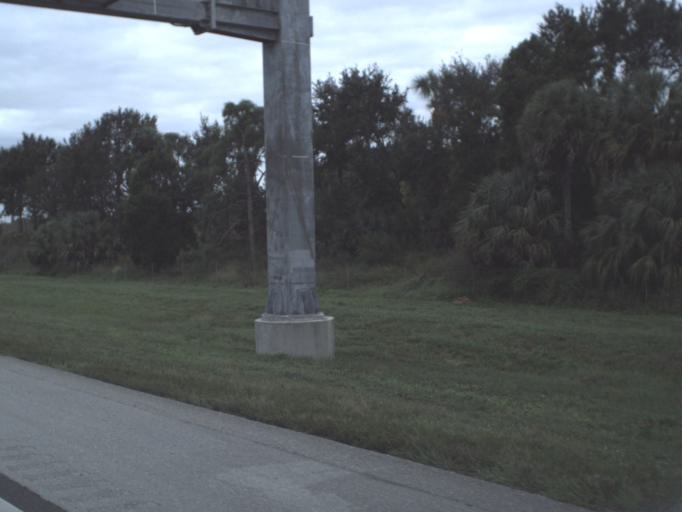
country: US
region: Florida
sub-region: Lee County
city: Bonita Springs
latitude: 26.2960
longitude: -81.7431
